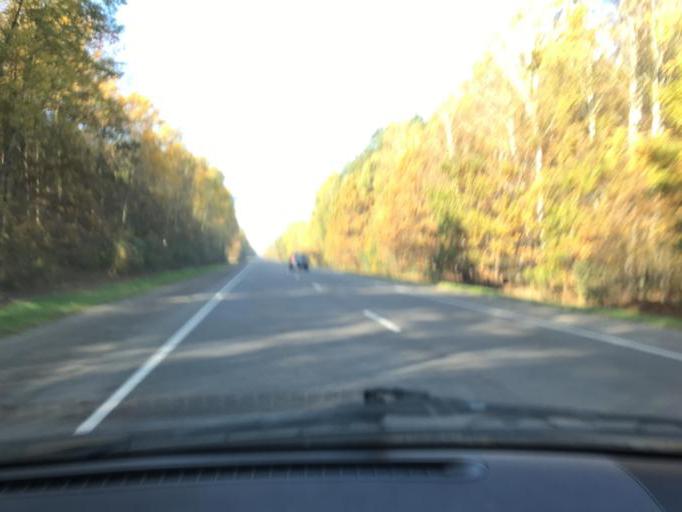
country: BY
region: Brest
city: Horad Luninyets
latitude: 52.2922
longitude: 26.7653
